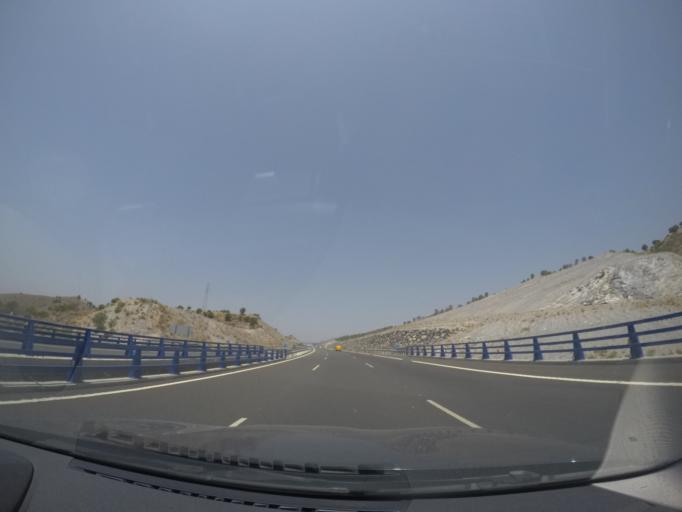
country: ES
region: Andalusia
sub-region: Provincia de Granada
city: Motril
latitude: 36.7715
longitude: -3.4882
